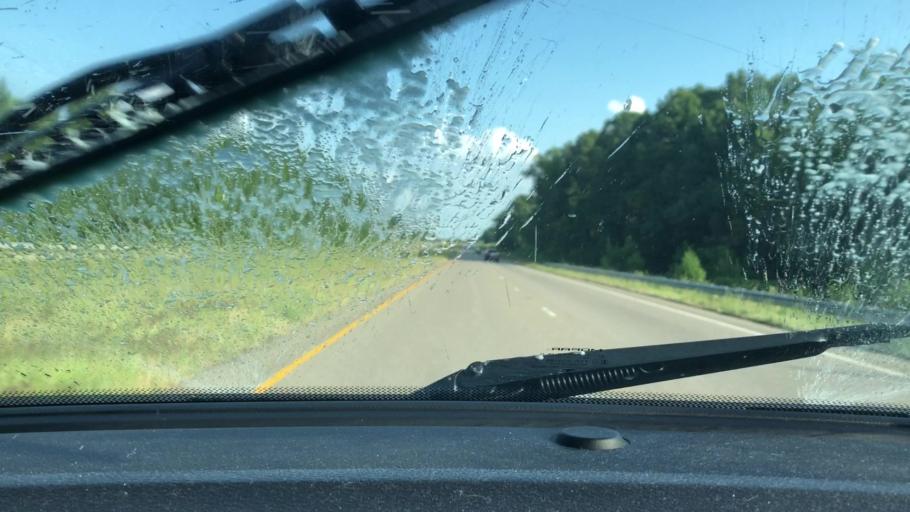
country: US
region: North Carolina
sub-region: Chatham County
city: Farmville
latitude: 35.5847
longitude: -79.3131
